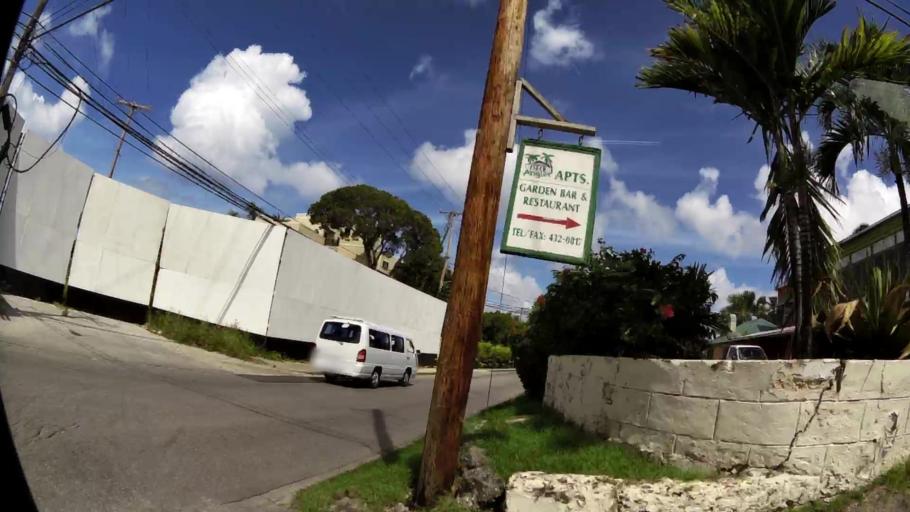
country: BB
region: Saint James
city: Holetown
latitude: 13.1562
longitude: -59.6365
